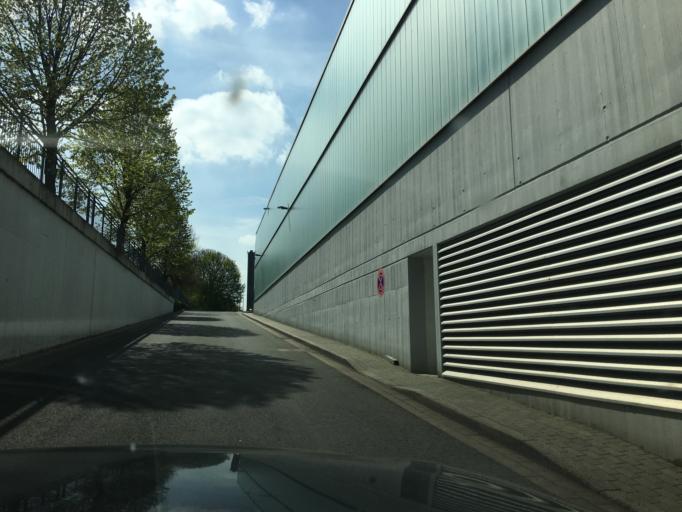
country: DE
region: North Rhine-Westphalia
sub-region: Regierungsbezirk Arnsberg
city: Holzwickede
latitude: 51.5126
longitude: 7.6089
